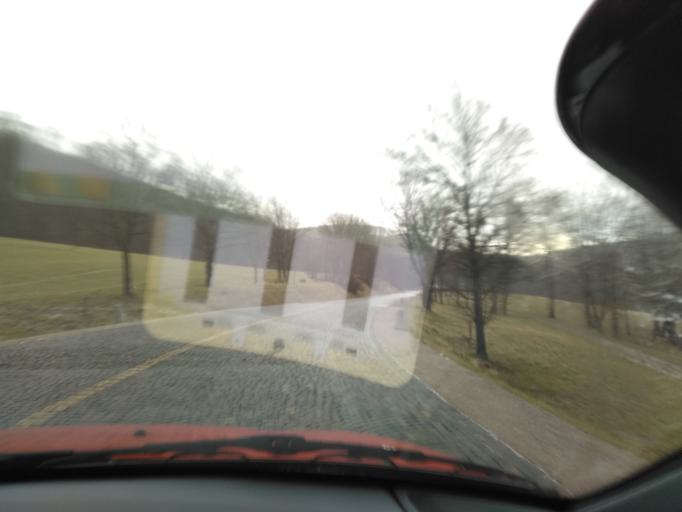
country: AT
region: Lower Austria
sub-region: Politischer Bezirk Wien-Umgebung
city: Klosterneuburg
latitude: 48.2660
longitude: 16.2943
